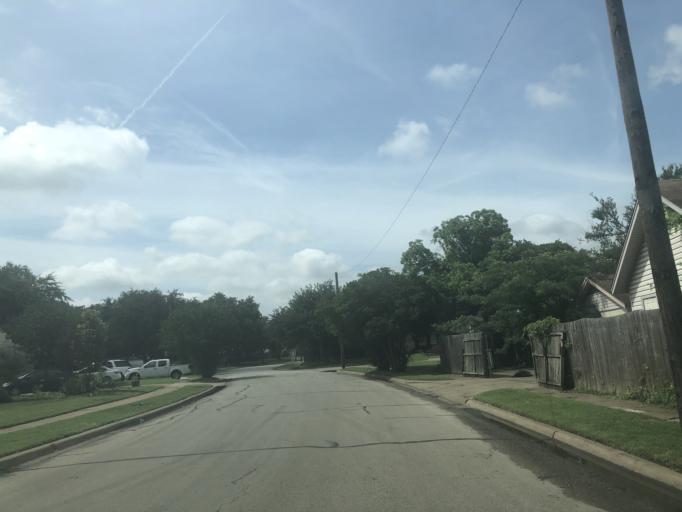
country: US
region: Texas
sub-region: Dallas County
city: Irving
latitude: 32.8024
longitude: -96.9739
